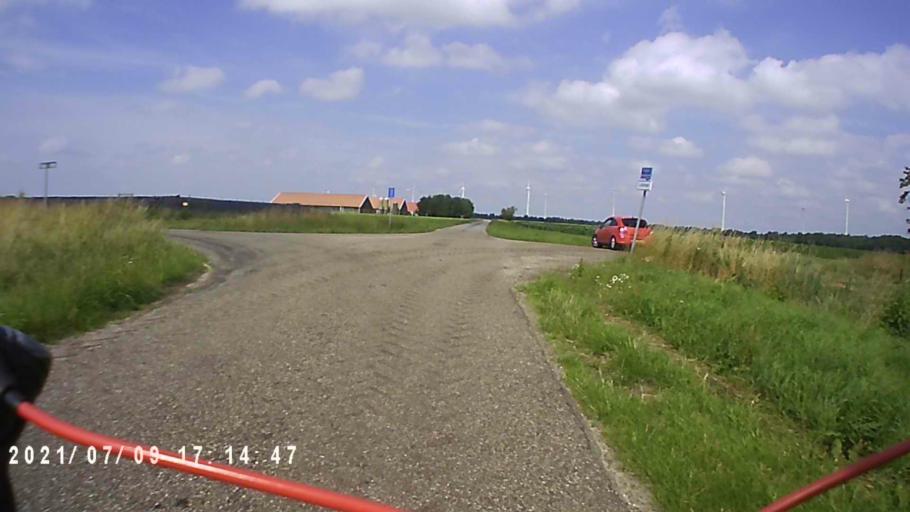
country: DE
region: Lower Saxony
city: Rhede
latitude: 53.0862
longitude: 7.1869
